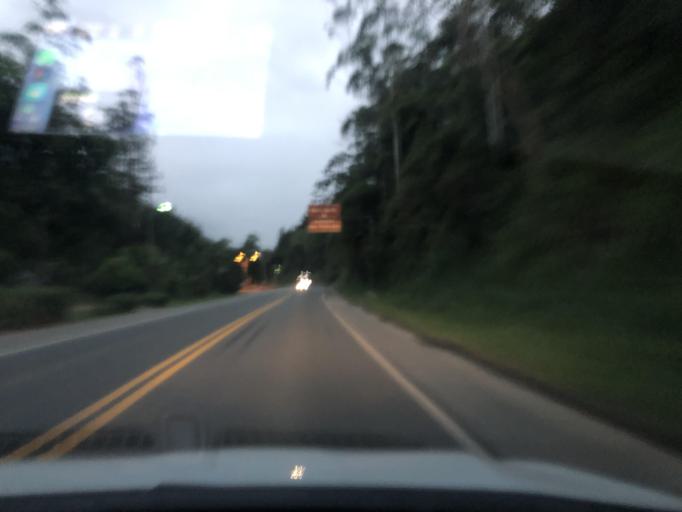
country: BR
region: Santa Catarina
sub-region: Pomerode
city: Pomerode
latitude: -26.6631
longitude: -49.0324
